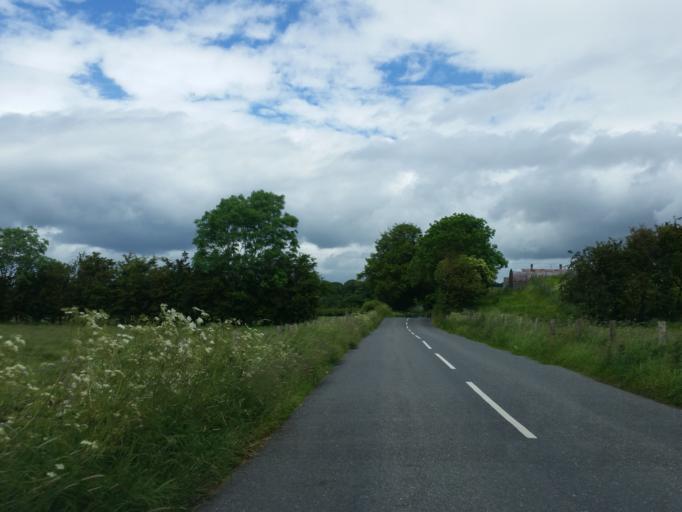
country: GB
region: Northern Ireland
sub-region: Omagh District
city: Omagh
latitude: 54.5496
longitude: -7.1180
